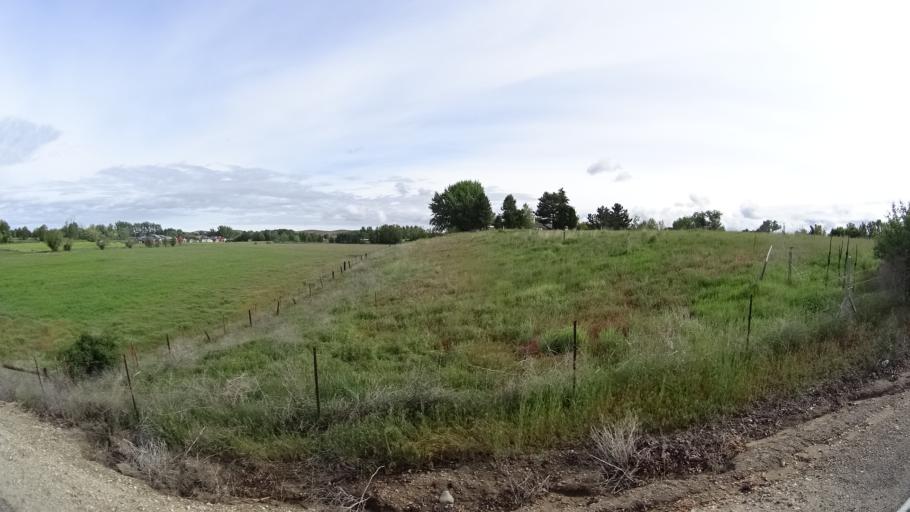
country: US
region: Idaho
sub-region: Ada County
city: Eagle
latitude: 43.7208
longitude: -116.3709
